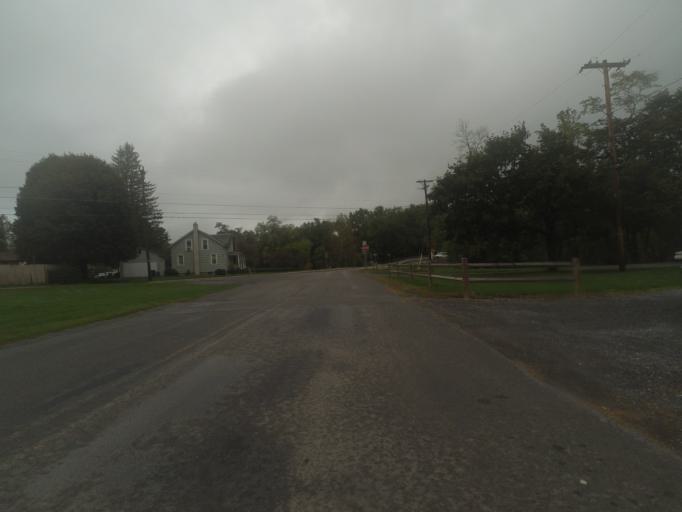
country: US
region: Pennsylvania
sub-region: Huntingdon County
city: McConnellstown
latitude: 40.5549
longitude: -78.0985
